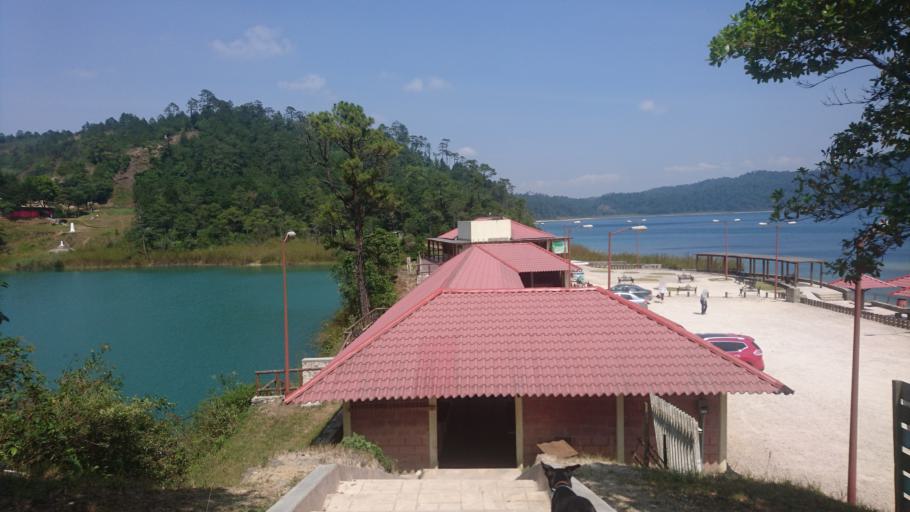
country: GT
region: Huehuetenango
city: Union
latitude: 16.0747
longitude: -91.6809
